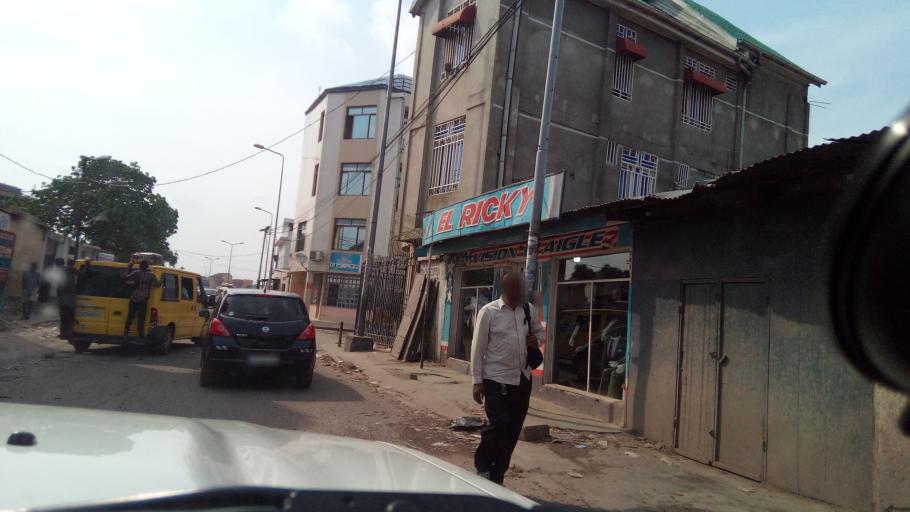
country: CD
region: Kinshasa
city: Kinshasa
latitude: -4.3504
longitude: 15.3230
